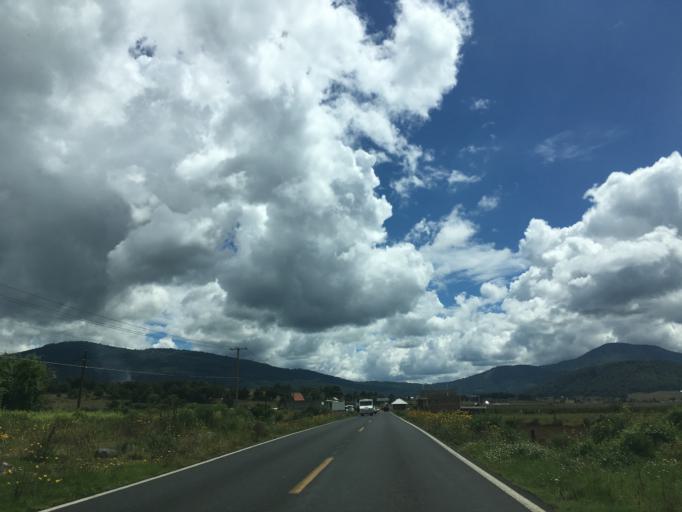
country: MX
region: Michoacan
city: Nahuatzen
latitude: 19.6649
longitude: -101.9394
